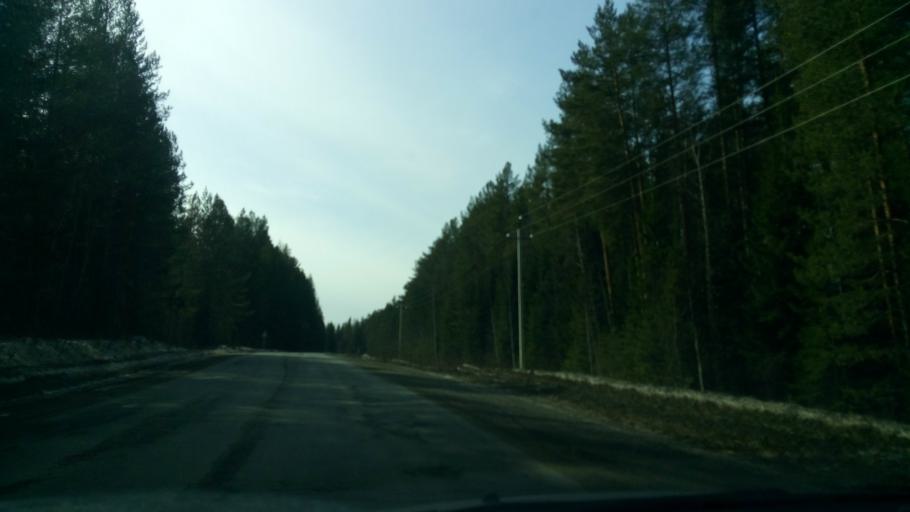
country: RU
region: Sverdlovsk
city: Chernoistochinsk
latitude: 57.7264
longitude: 59.7861
